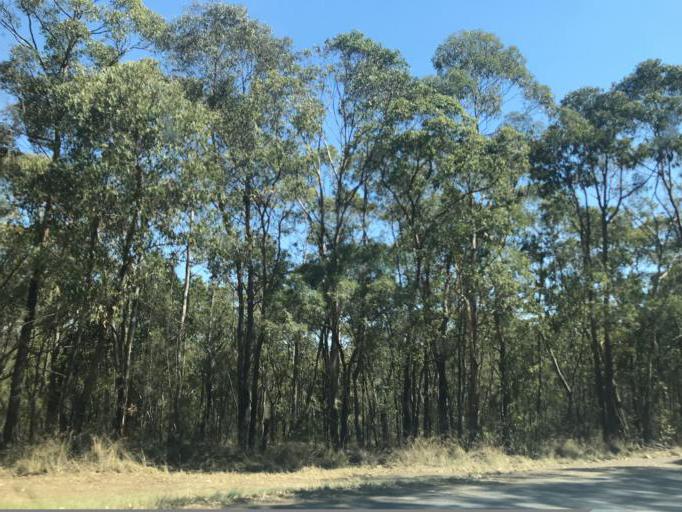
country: AU
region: New South Wales
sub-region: Hawkesbury
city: Pitt Town
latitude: -33.4642
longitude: 150.8494
